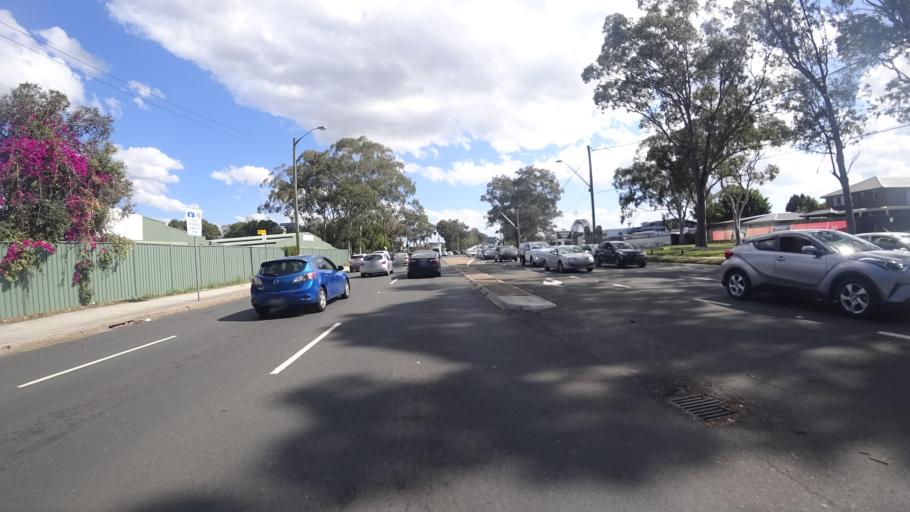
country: AU
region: New South Wales
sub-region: Fairfield
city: Liverpool
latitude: -33.9107
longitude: 150.9394
